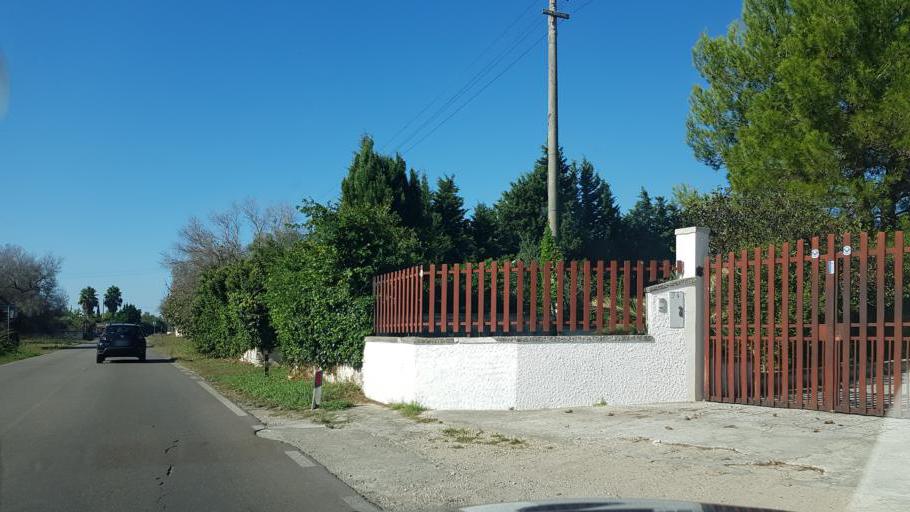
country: IT
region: Apulia
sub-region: Provincia di Lecce
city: Magliano
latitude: 40.3188
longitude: 18.0638
